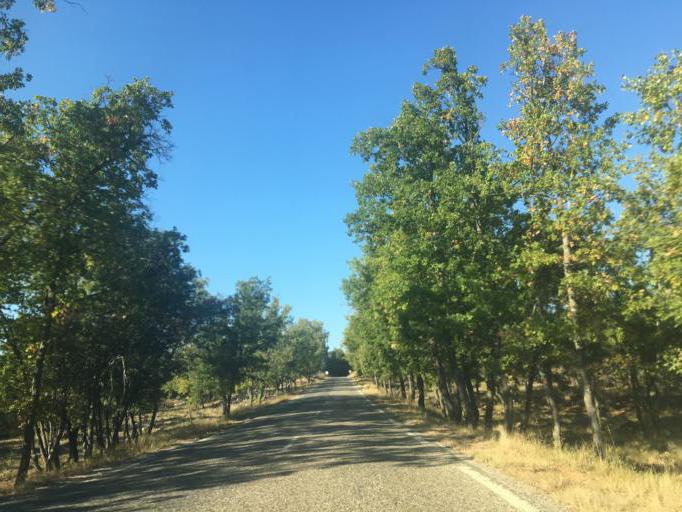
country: FR
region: Provence-Alpes-Cote d'Azur
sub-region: Departement du Var
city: Aups
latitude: 43.6095
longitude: 6.2188
